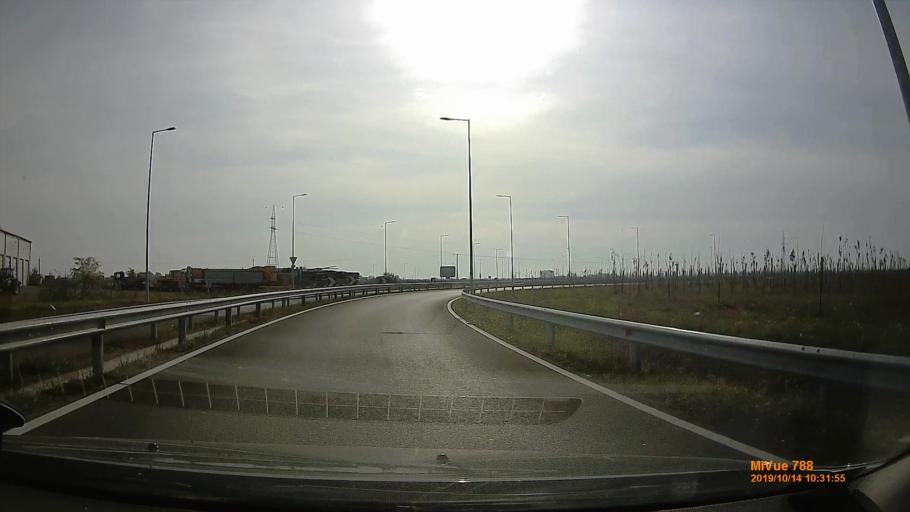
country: HU
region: Pest
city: Cegled
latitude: 47.1979
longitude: 19.8154
